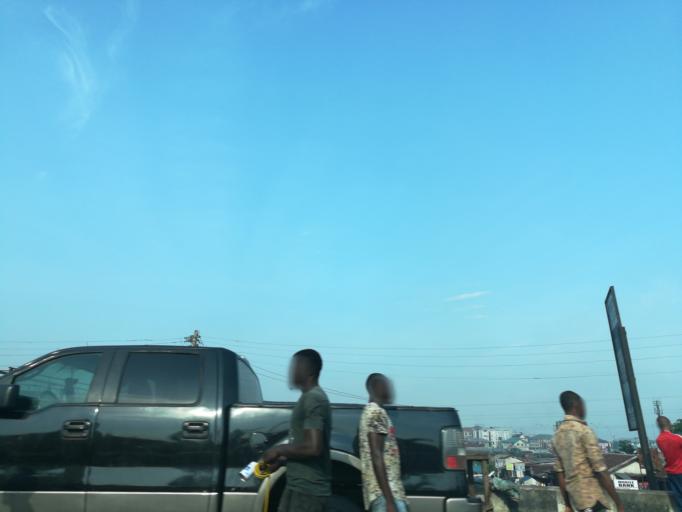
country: NG
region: Rivers
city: Port Harcourt
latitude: 4.8211
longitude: 7.0238
